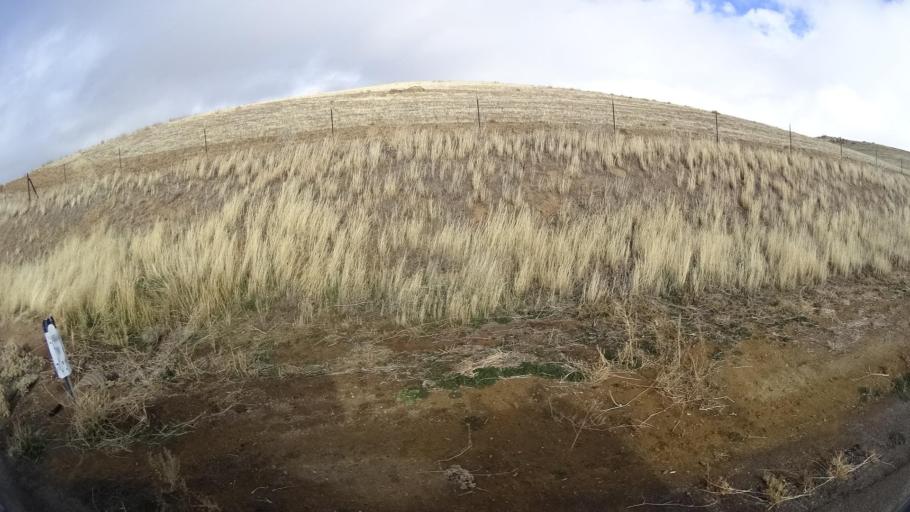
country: US
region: California
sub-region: Kern County
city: Maricopa
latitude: 34.9075
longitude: -119.3913
